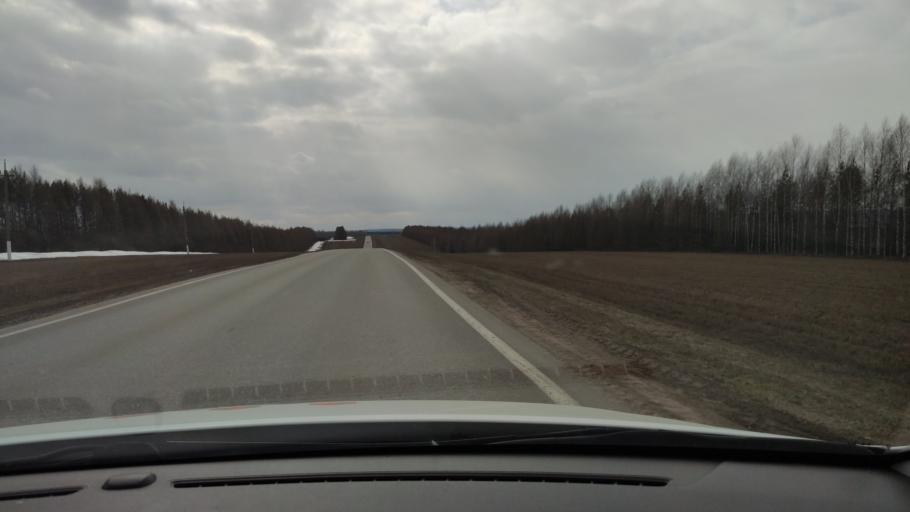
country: RU
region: Tatarstan
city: Vysokaya Gora
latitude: 56.2253
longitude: 49.2897
